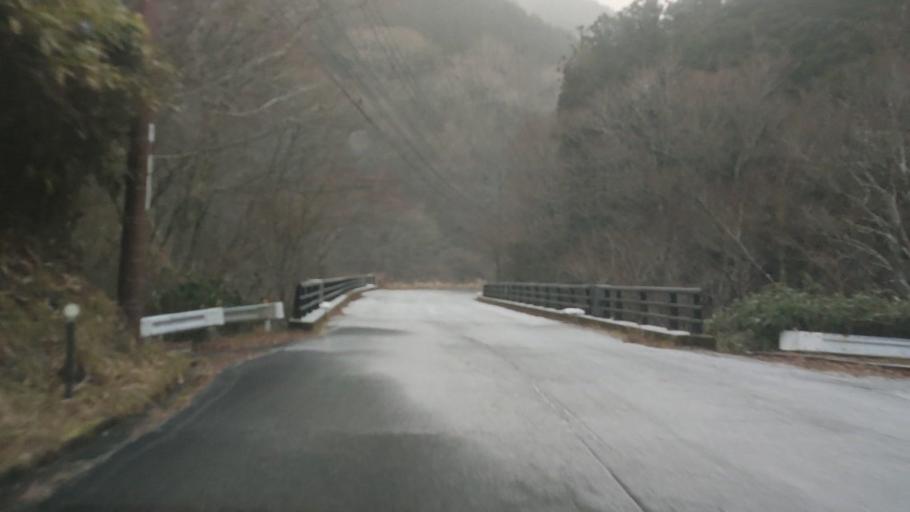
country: JP
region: Kumamoto
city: Matsubase
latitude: 32.5653
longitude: 130.9123
